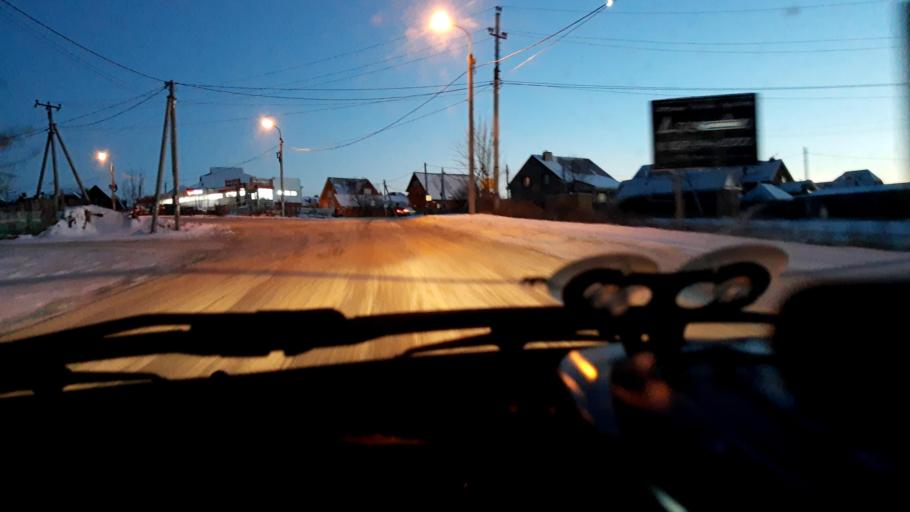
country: RU
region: Bashkortostan
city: Ufa
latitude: 54.6057
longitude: 55.9436
